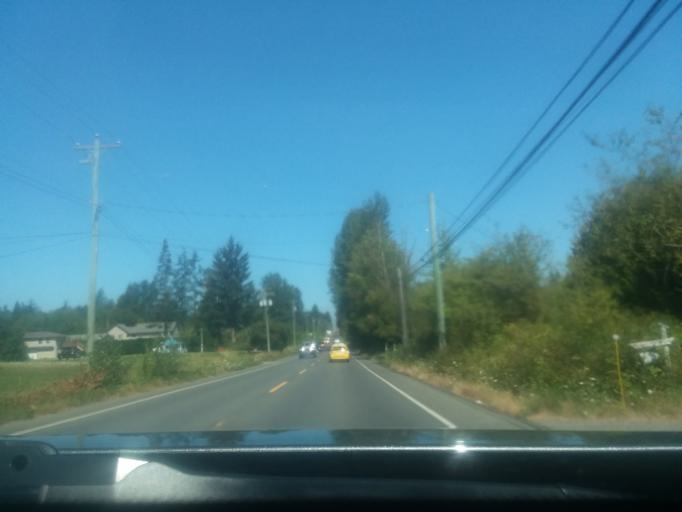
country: CA
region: British Columbia
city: Courtenay
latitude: 49.6924
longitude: -124.9347
